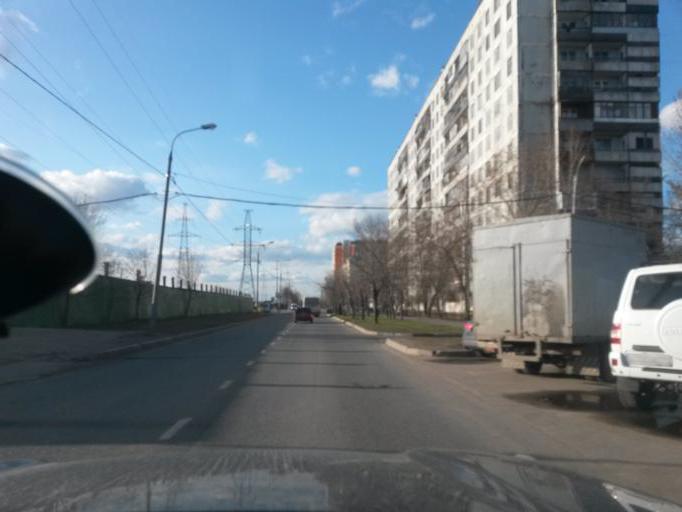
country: RU
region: Moskovskaya
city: Biryulevo Zapadnoye
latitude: 55.5792
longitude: 37.6428
